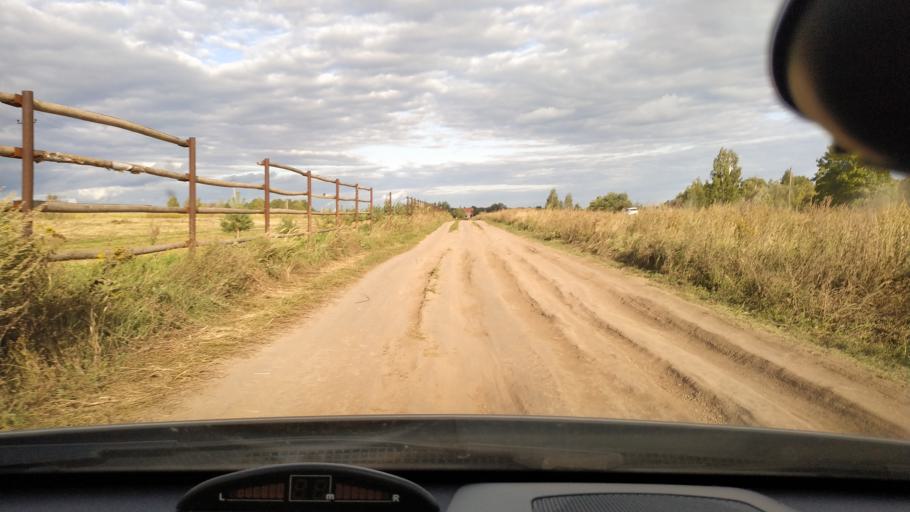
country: RU
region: Rjazan
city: Polyany
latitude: 54.5648
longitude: 39.8693
